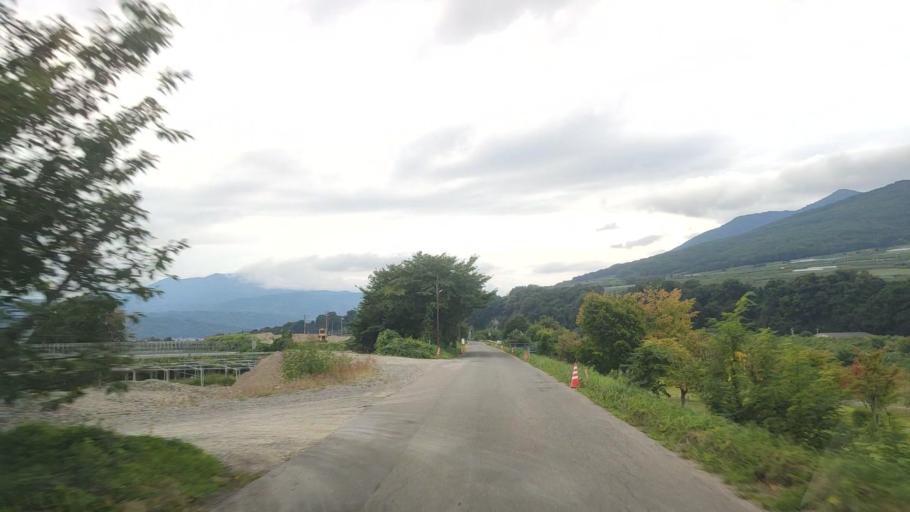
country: JP
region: Nagano
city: Nakano
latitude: 36.7651
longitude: 138.3941
